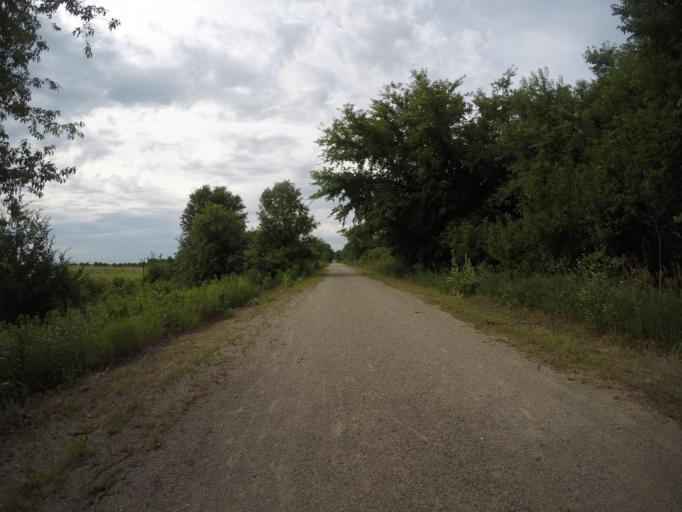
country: US
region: Kansas
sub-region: Anderson County
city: Garnett
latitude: 38.4294
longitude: -95.2635
